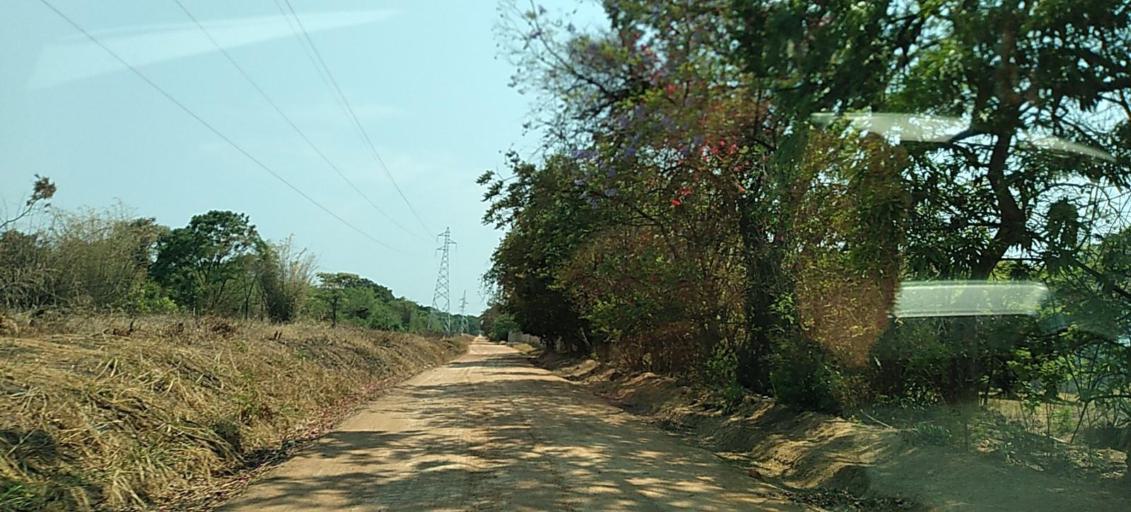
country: ZM
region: Copperbelt
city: Chambishi
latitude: -12.6163
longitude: 27.9502
